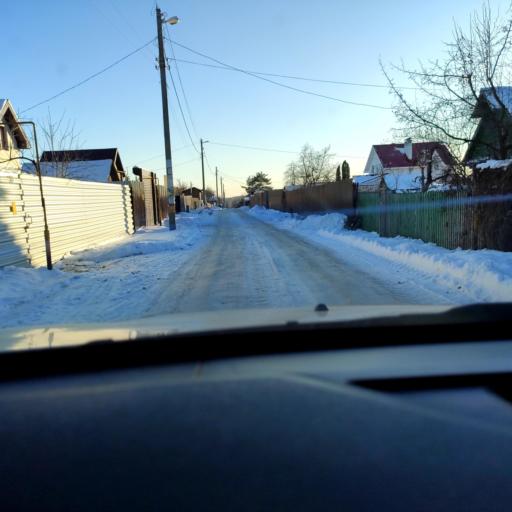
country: RU
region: Samara
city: Petra-Dubrava
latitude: 53.2846
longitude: 50.2917
